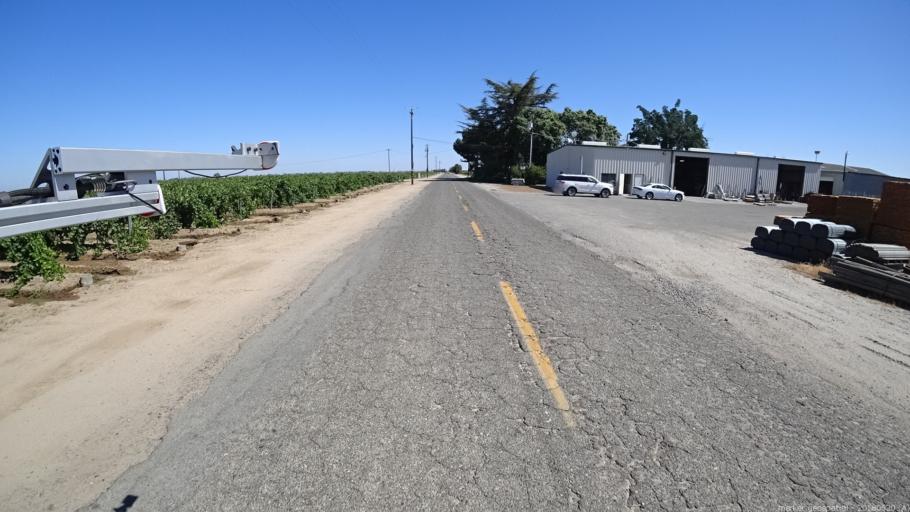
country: US
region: California
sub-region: Fresno County
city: Biola
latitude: 36.8596
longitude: -120.0193
